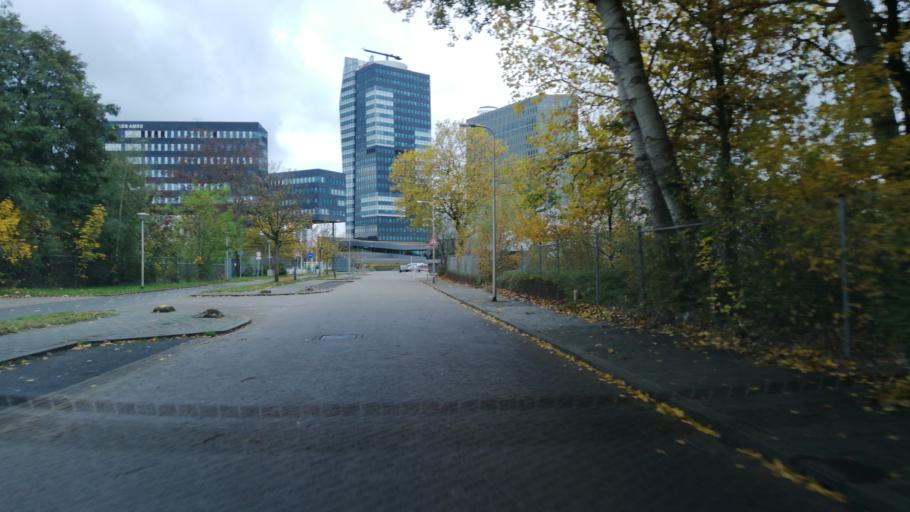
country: NL
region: Overijssel
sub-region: Gemeente Zwolle
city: Zwolle
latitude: 52.5106
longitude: 6.0693
